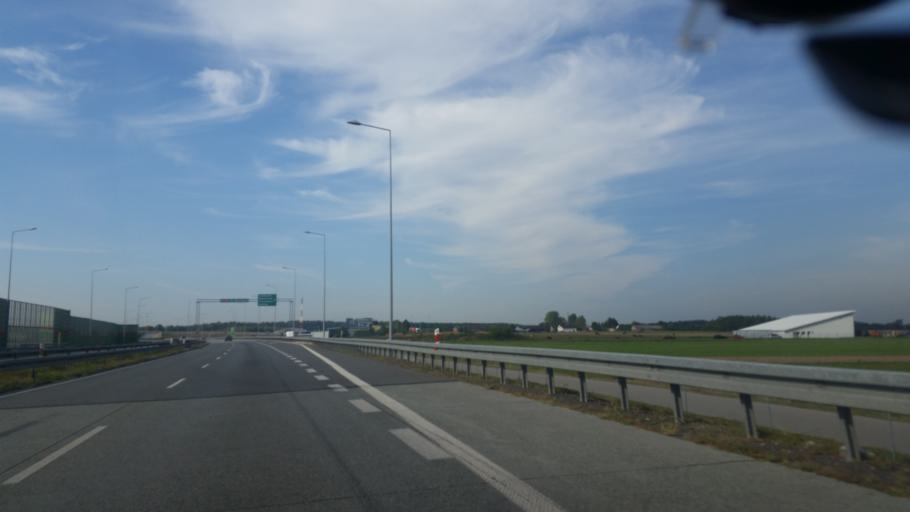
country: PL
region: Lodz Voivodeship
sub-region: Powiat tomaszowski
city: Czerniewice
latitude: 51.6585
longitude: 20.1595
